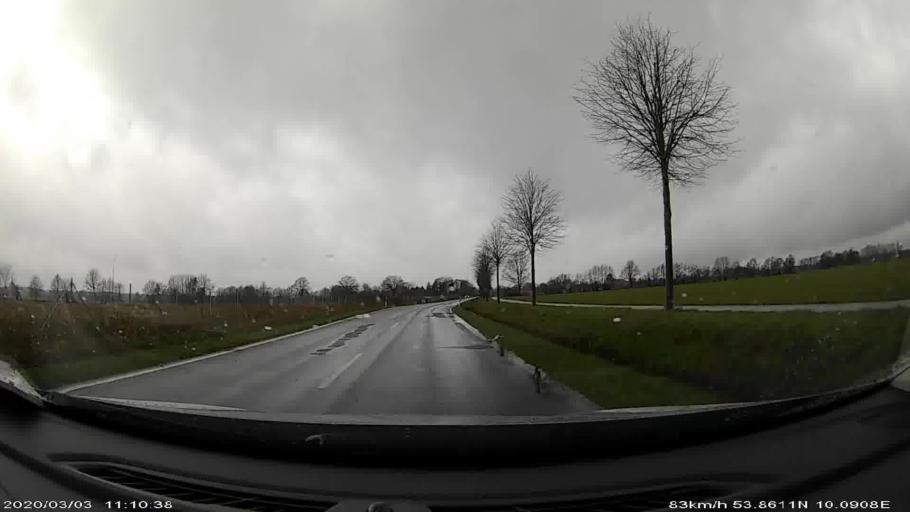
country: DE
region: Schleswig-Holstein
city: Sievershutten
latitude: 53.8629
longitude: 10.0858
